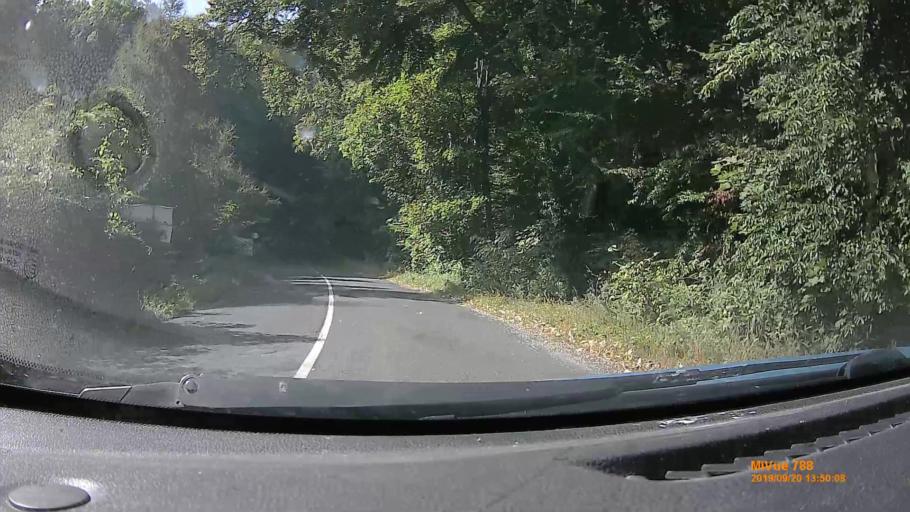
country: HU
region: Borsod-Abauj-Zemplen
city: Saly
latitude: 48.0670
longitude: 20.5909
